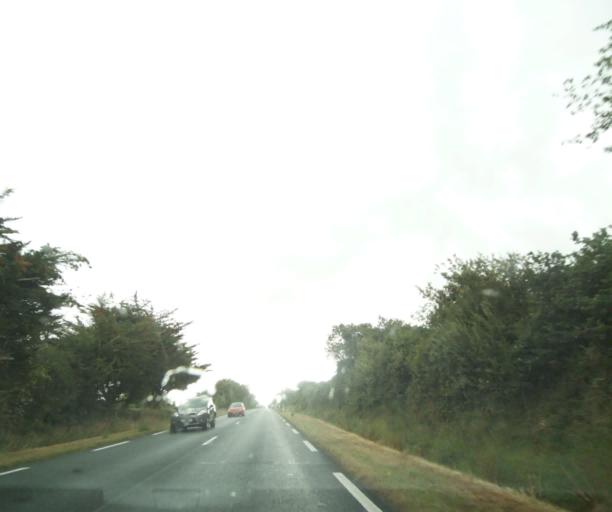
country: FR
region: Pays de la Loire
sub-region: Departement de la Vendee
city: Chateau-d'Olonne
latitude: 46.4796
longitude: -1.6962
